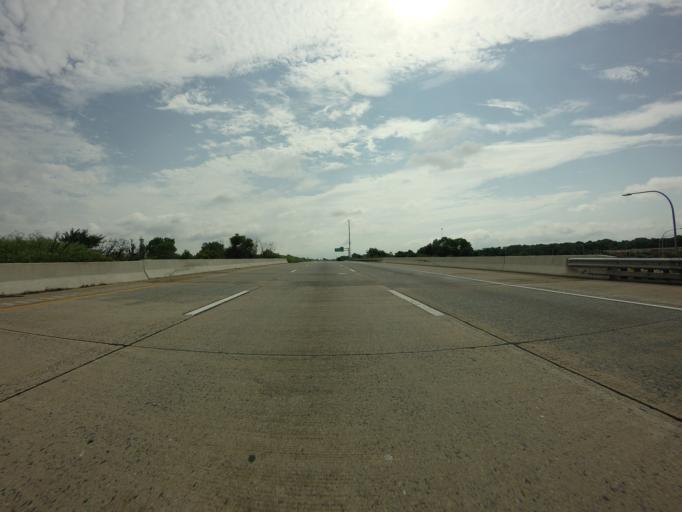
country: US
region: Delaware
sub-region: New Castle County
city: Wilmington
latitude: 39.7169
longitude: -75.5602
